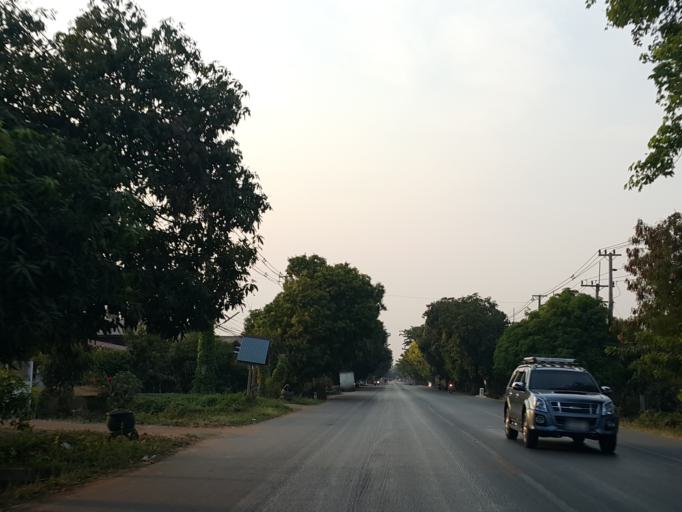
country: TH
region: Sukhothai
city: Si Samrong
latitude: 17.2199
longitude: 99.8625
